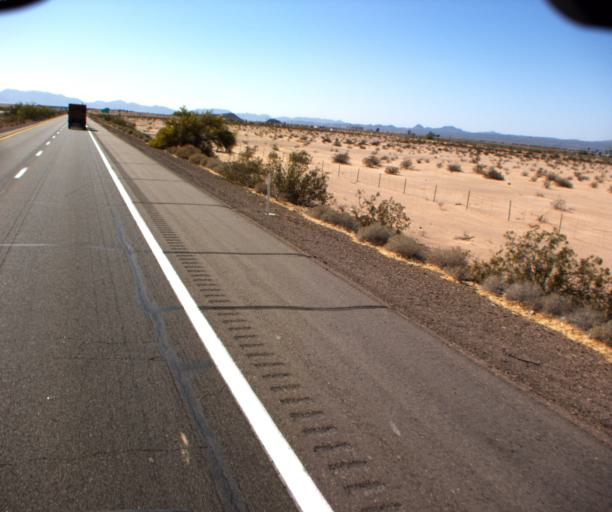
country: US
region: Arizona
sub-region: Yuma County
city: Wellton
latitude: 32.6840
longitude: -114.0114
